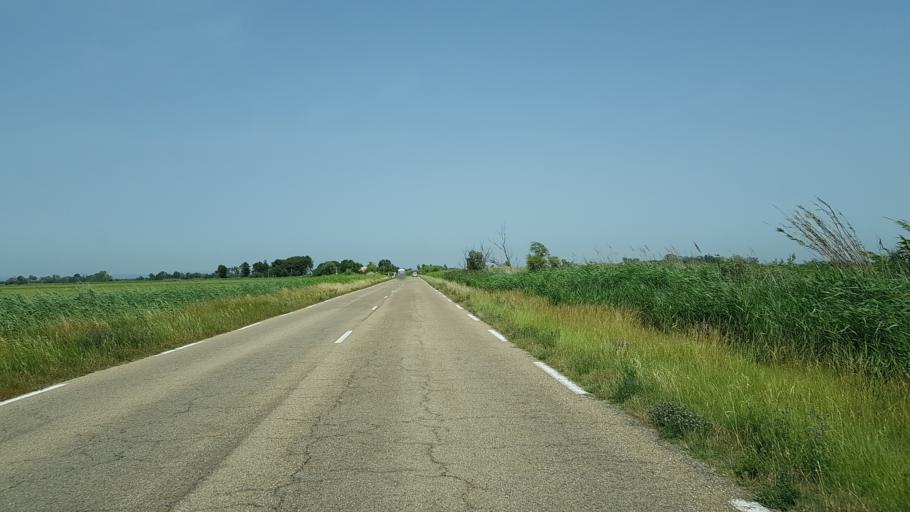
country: FR
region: Provence-Alpes-Cote d'Azur
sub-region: Departement des Bouches-du-Rhone
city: Port-Saint-Louis-du-Rhone
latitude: 43.4665
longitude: 4.7637
